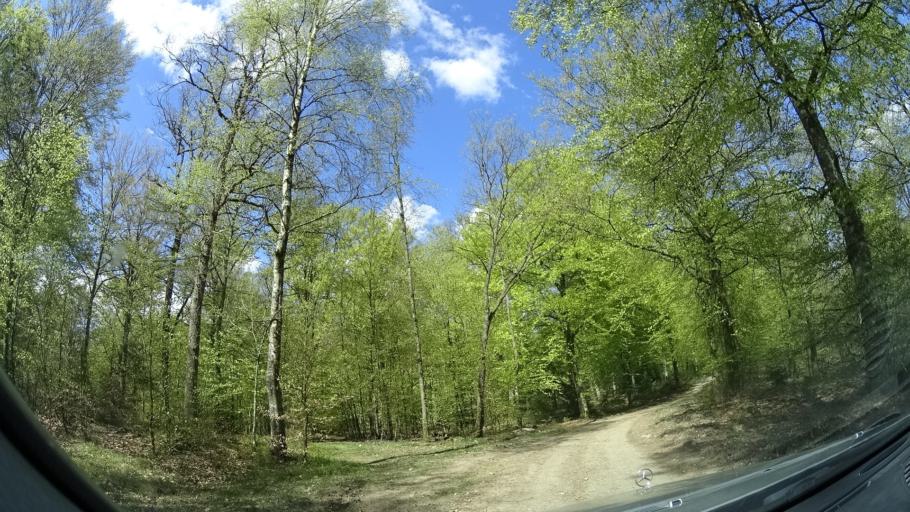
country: SE
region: Skane
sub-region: Hassleholms Kommun
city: Tormestorp
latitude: 56.0930
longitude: 13.6918
